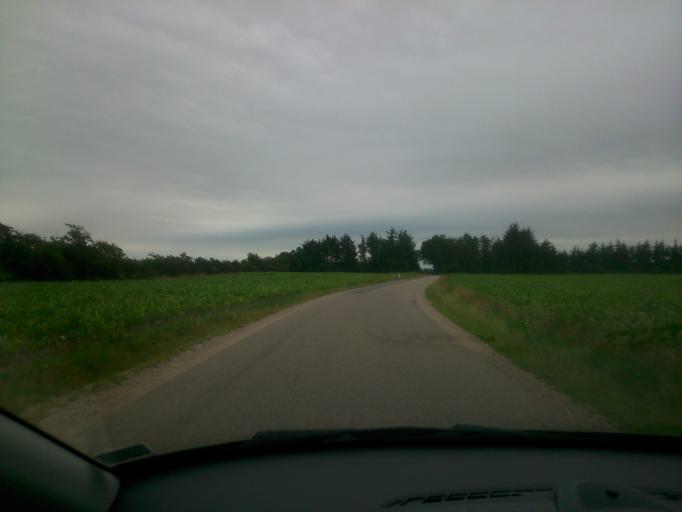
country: DK
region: Central Jutland
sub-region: Ringkobing-Skjern Kommune
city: Skjern
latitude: 55.9795
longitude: 8.3756
